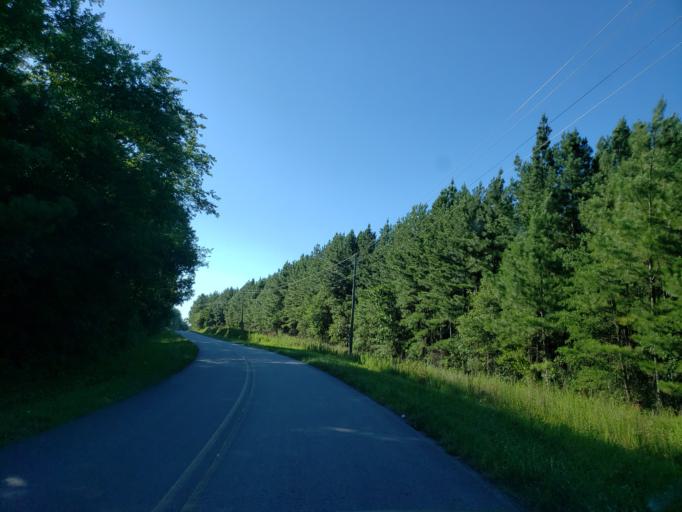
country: US
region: Georgia
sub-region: Bartow County
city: Euharlee
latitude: 34.1087
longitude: -85.0034
